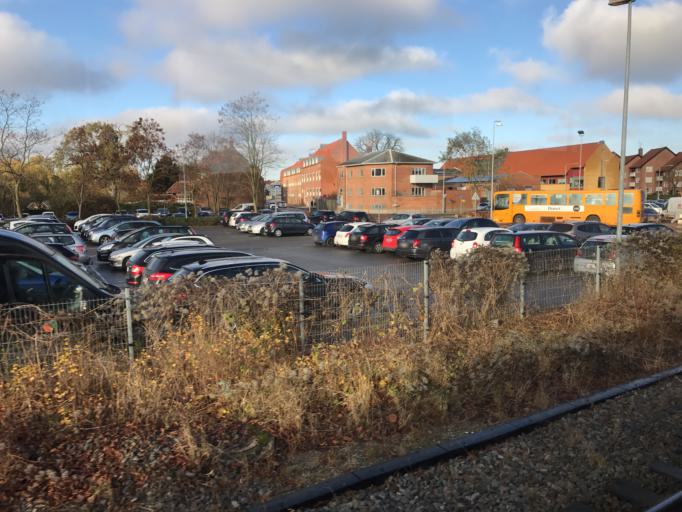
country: DK
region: Zealand
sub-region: Koge Kommune
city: Koge
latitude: 55.4533
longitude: 12.1849
